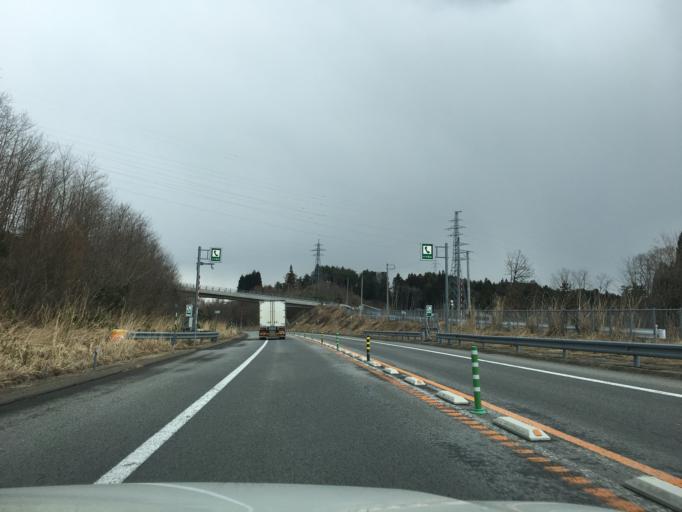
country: JP
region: Aomori
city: Aomori Shi
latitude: 40.7998
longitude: 140.6996
